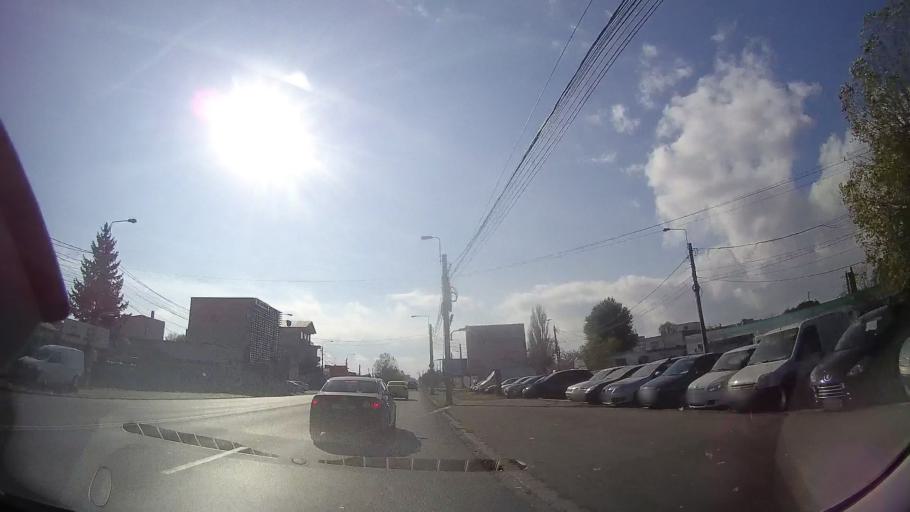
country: RO
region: Constanta
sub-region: Municipiul Constanta
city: Constanta
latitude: 44.1531
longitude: 28.6282
